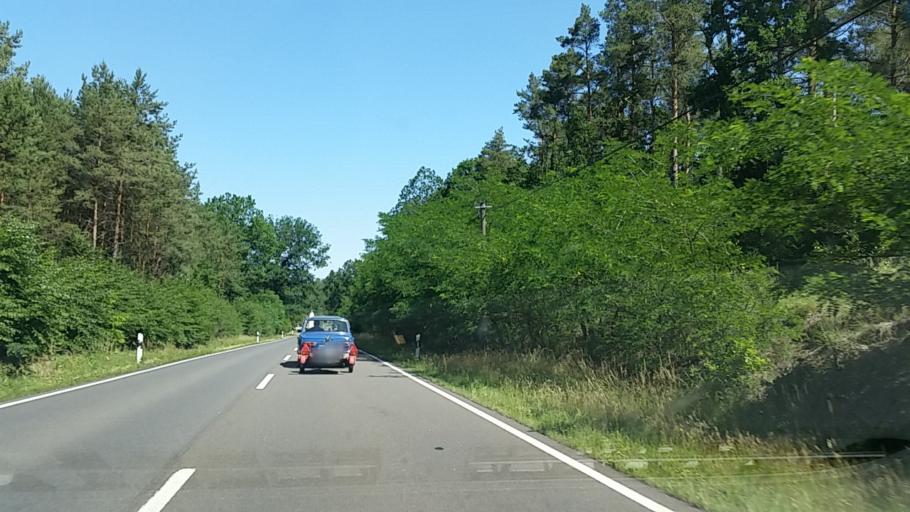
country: DE
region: Saxony-Anhalt
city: Kemberg
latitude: 51.7154
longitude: 12.6181
